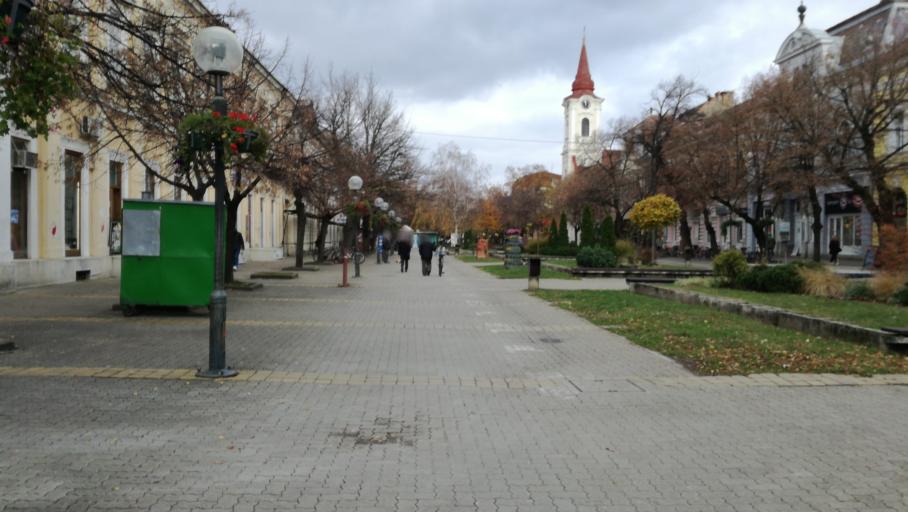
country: RS
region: Autonomna Pokrajina Vojvodina
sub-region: Severnobanatski Okrug
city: Kikinda
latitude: 45.8305
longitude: 20.4661
